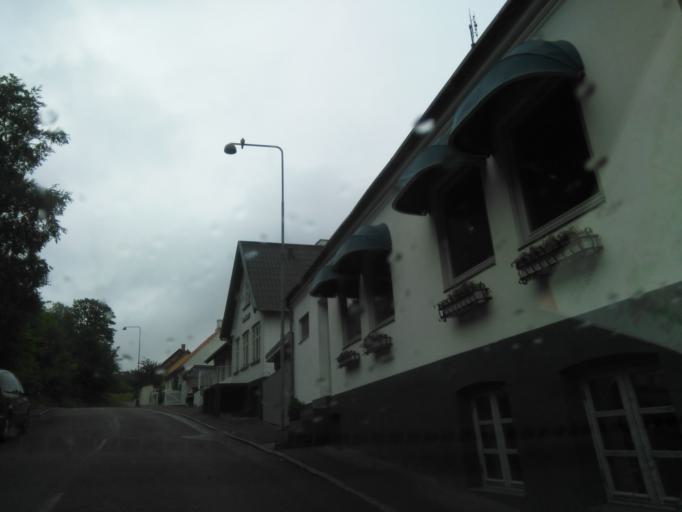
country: DK
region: Capital Region
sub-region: Bornholm Kommune
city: Ronne
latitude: 55.2485
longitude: 14.7383
